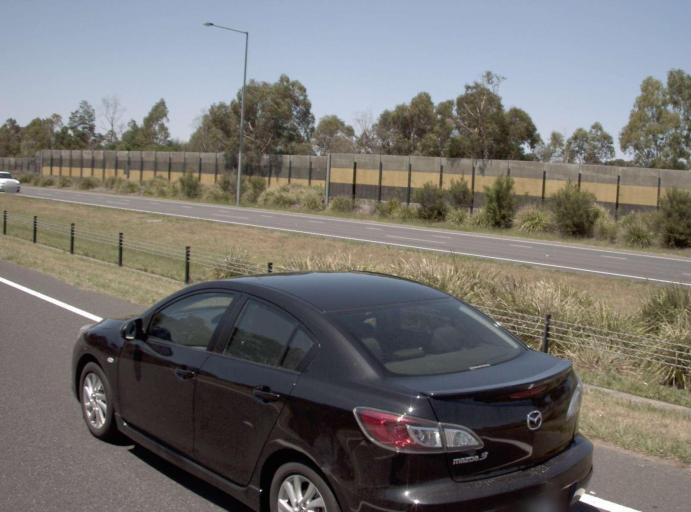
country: AU
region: Victoria
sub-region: Casey
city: Narre Warren
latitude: -38.0238
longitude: 145.3163
